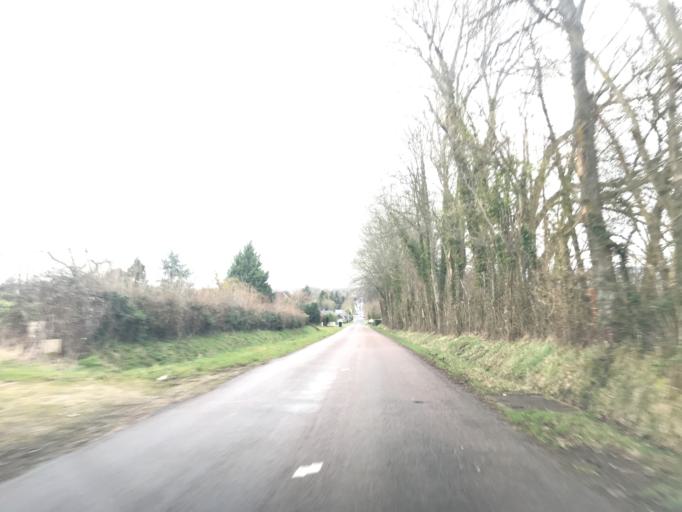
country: FR
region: Lower Normandy
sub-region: Departement du Calvados
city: Touques
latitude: 49.2719
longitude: 0.1080
